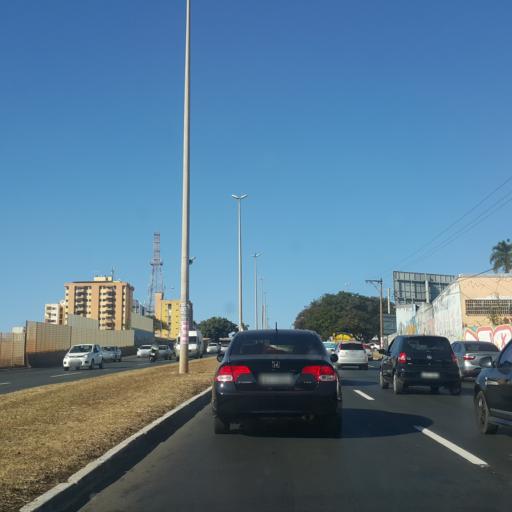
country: BR
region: Federal District
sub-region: Brasilia
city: Brasilia
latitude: -15.8356
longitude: -48.0628
